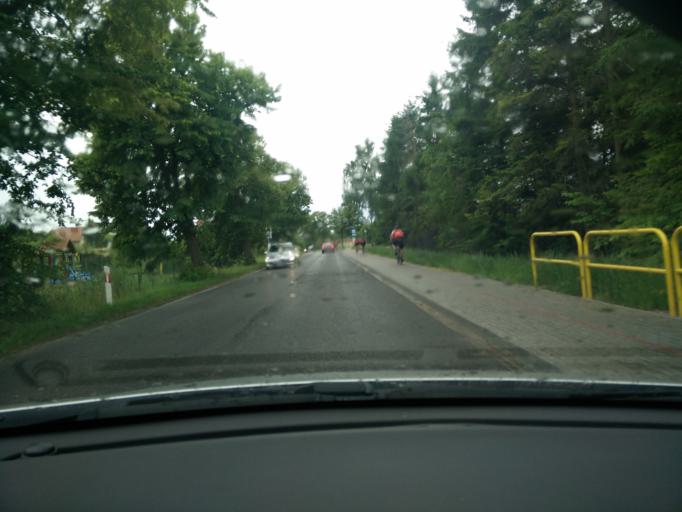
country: PL
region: Pomeranian Voivodeship
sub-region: Powiat pucki
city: Mosty
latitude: 54.6143
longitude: 18.4960
